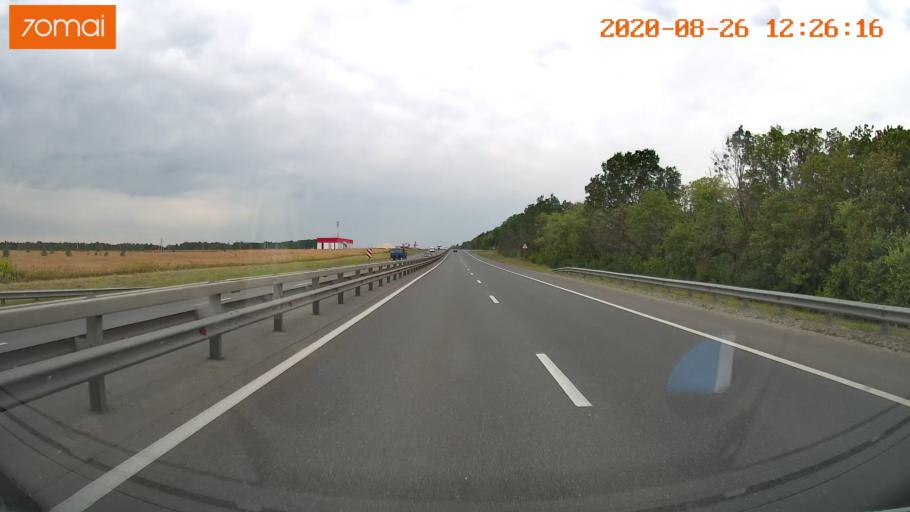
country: RU
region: Rjazan
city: Polyany
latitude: 54.5334
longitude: 39.8632
